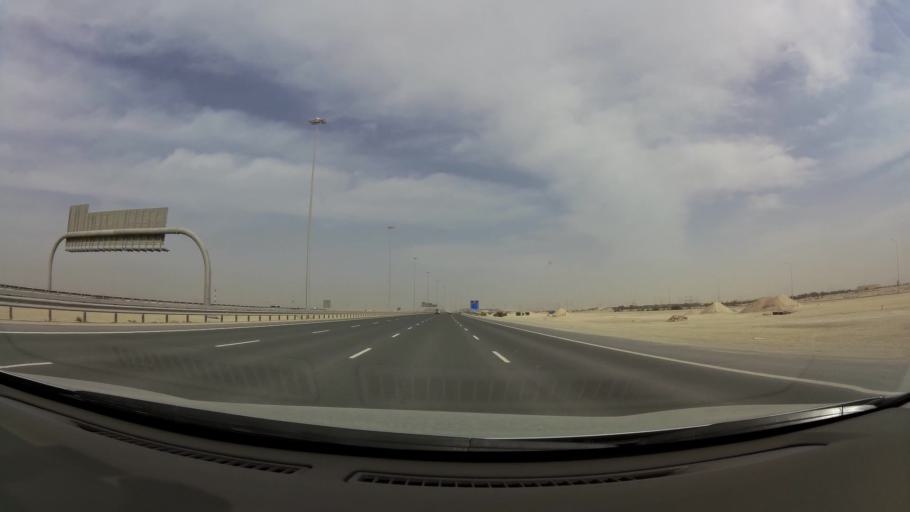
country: QA
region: Baladiyat ar Rayyan
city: Ash Shahaniyah
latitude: 25.3526
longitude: 51.2883
